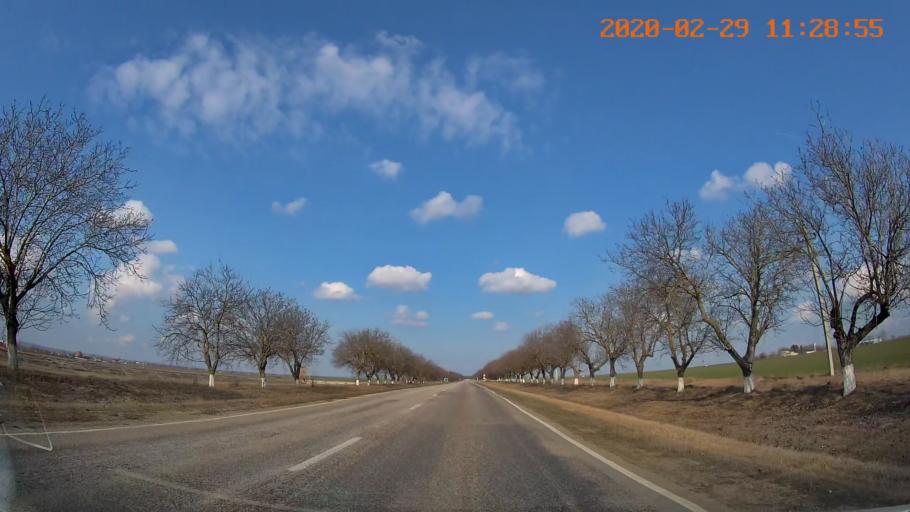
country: MD
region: Telenesti
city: Cocieri
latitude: 47.4865
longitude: 29.1299
